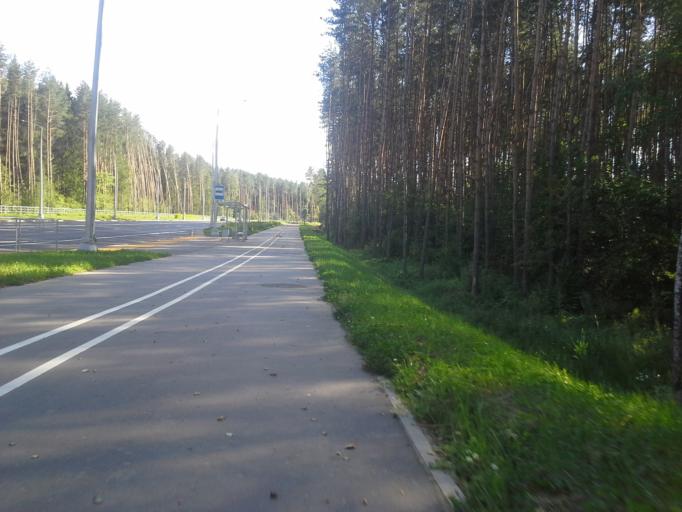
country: RU
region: Moskovskaya
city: Kokoshkino
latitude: 55.5745
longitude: 37.1635
